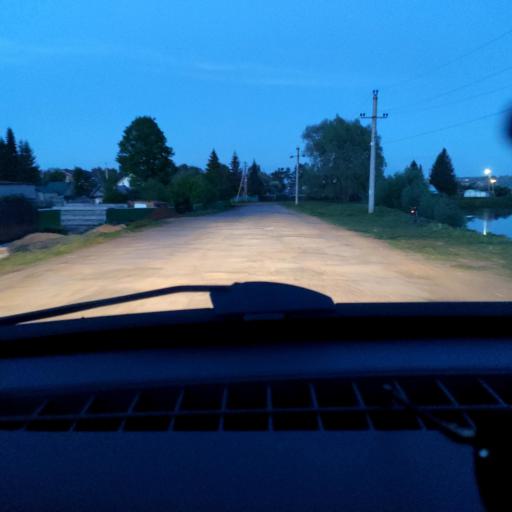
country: RU
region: Bashkortostan
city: Karmaskaly
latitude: 54.3690
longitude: 56.1611
